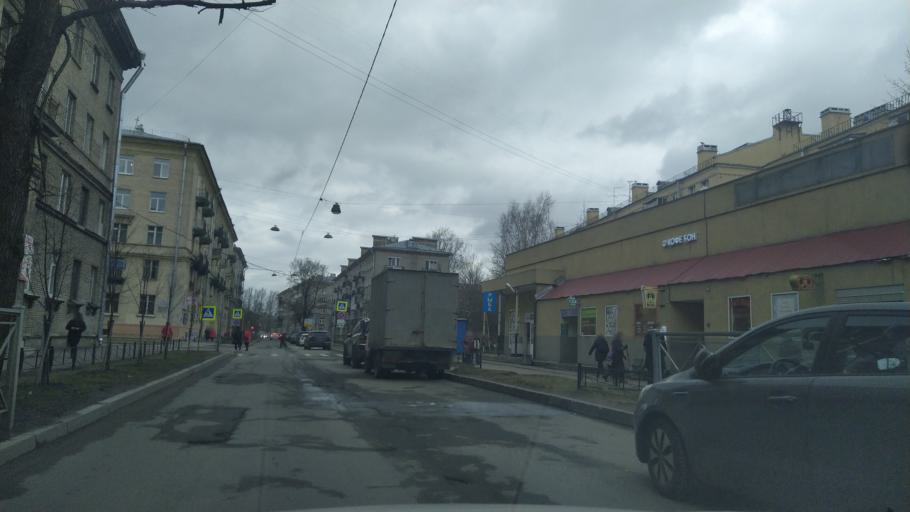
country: RU
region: St.-Petersburg
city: Novaya Derevnya
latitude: 59.9867
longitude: 30.2951
